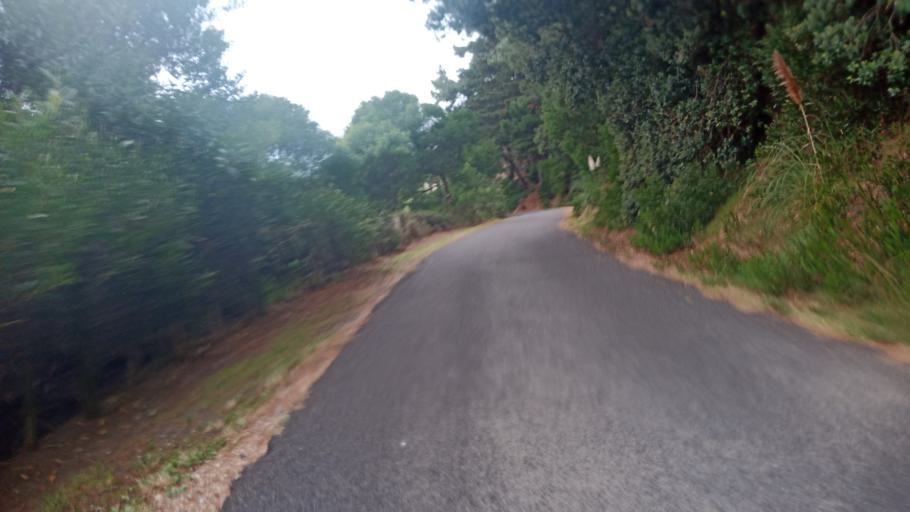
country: NZ
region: Gisborne
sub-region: Gisborne District
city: Gisborne
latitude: -38.6816
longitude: 178.0366
